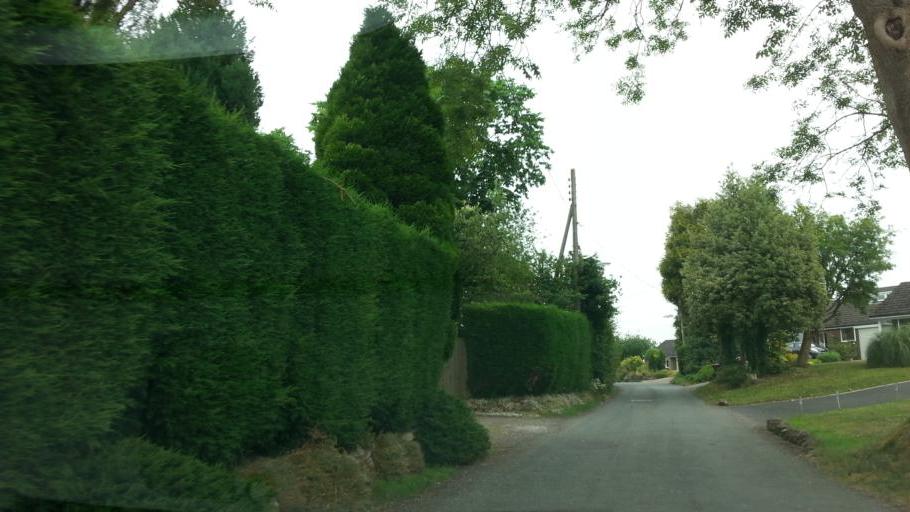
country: GB
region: England
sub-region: Staffordshire
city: Colwich
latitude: 52.8433
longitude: -1.9968
